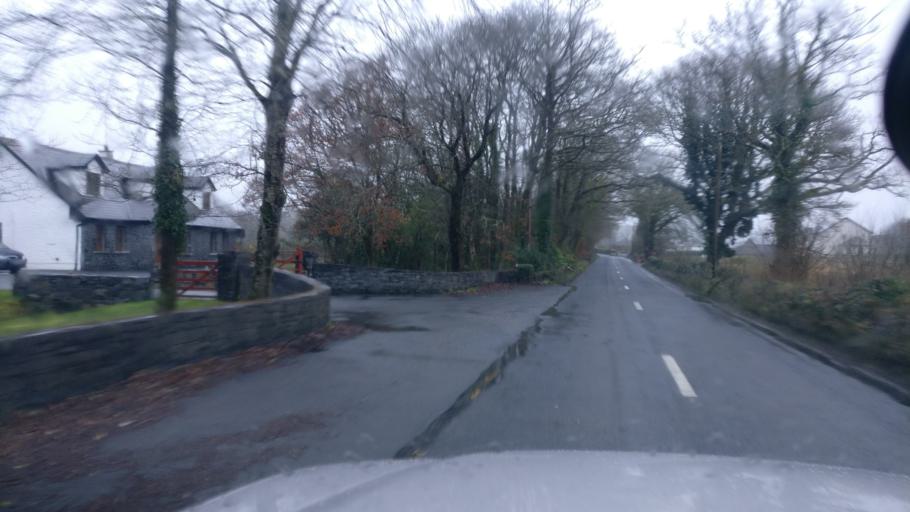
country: IE
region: Connaught
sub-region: County Galway
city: Loughrea
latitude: 53.1309
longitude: -8.4553
